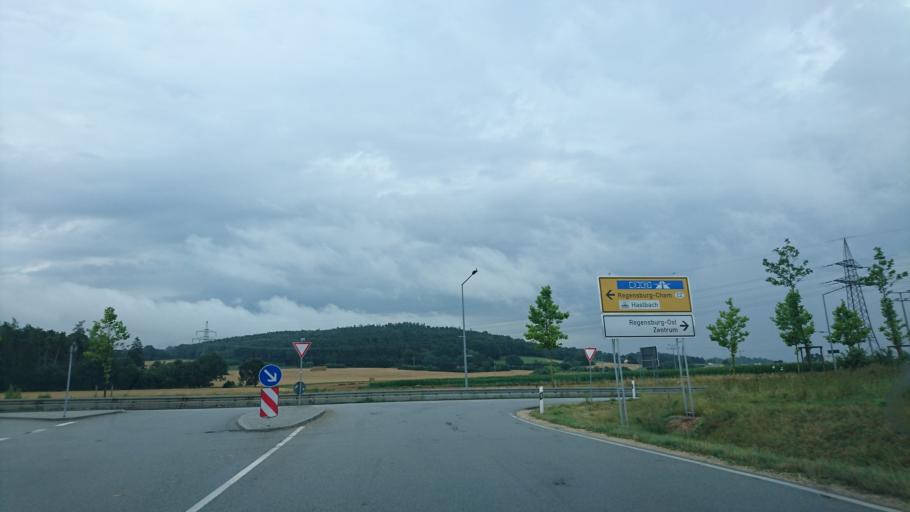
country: DE
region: Bavaria
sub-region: Upper Palatinate
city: Regensburg
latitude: 49.0538
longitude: 12.1322
